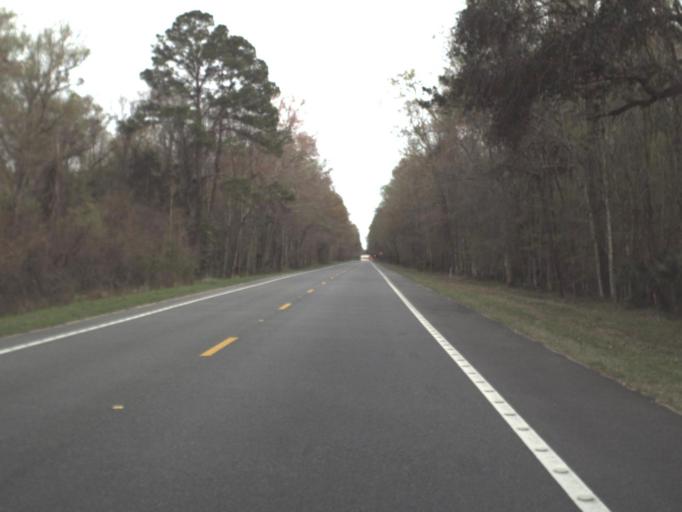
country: US
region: Florida
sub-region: Leon County
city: Woodville
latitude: 30.1545
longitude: -83.9910
